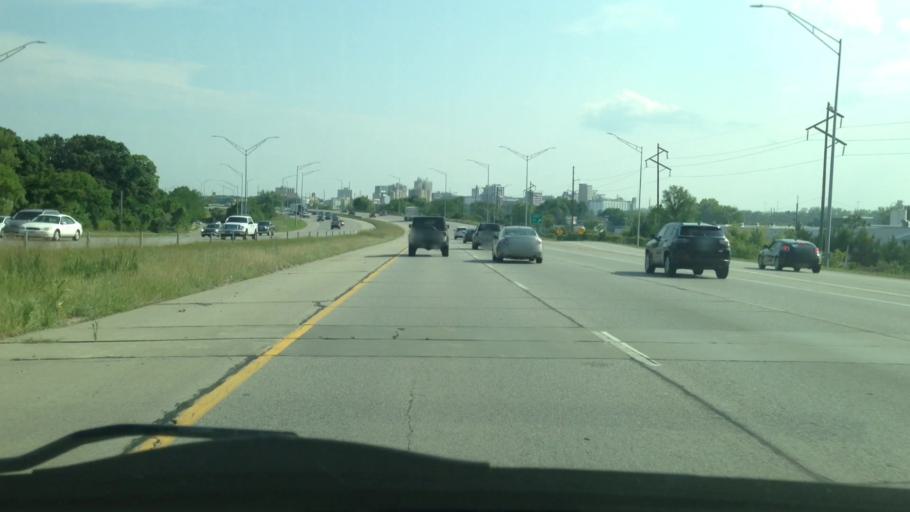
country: US
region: Iowa
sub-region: Linn County
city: Cedar Rapids
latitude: 41.9994
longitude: -91.6669
